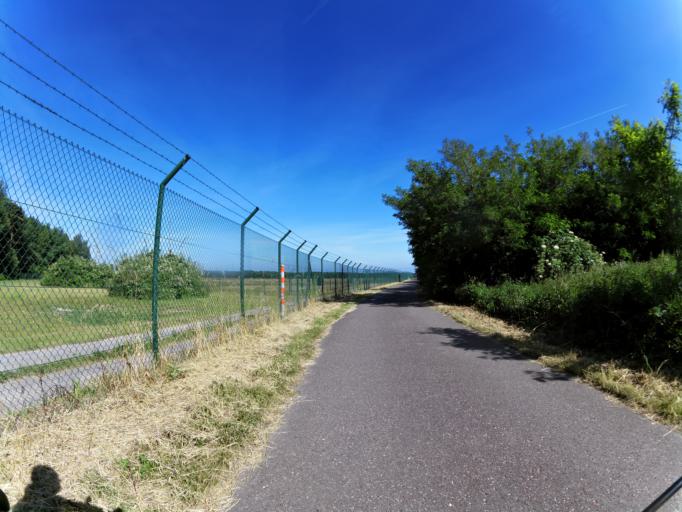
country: DE
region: North Rhine-Westphalia
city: Geilenkirchen
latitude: 50.9584
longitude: 6.0674
